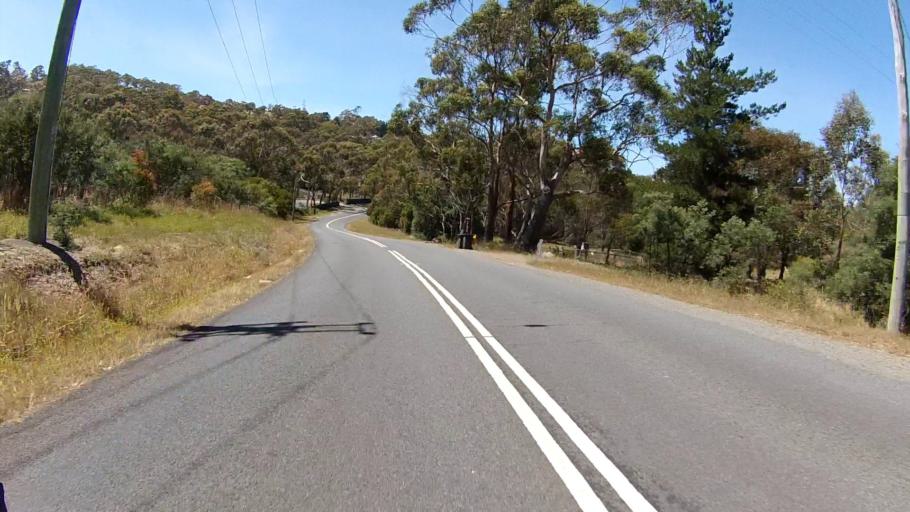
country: AU
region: Tasmania
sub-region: Clarence
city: Howrah
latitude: -42.8647
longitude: 147.4206
